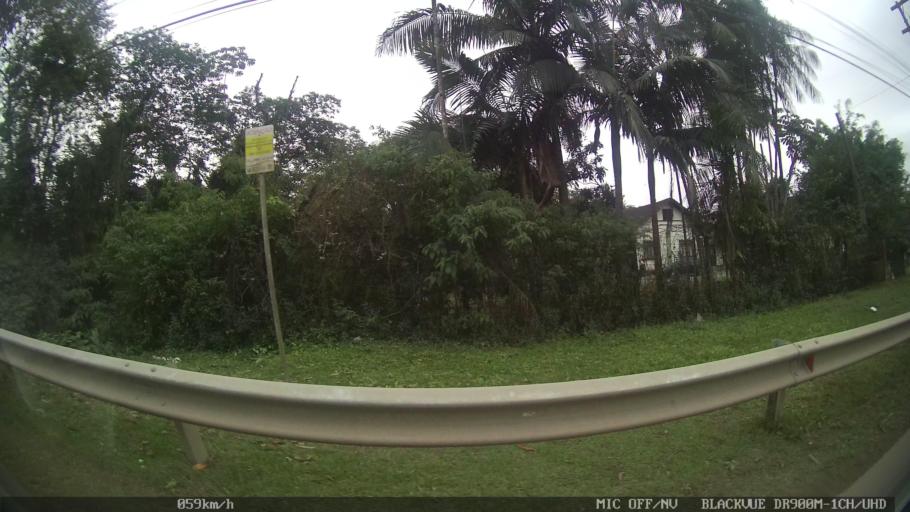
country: BR
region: Santa Catarina
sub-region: Joinville
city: Joinville
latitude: -26.2334
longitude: -48.8970
